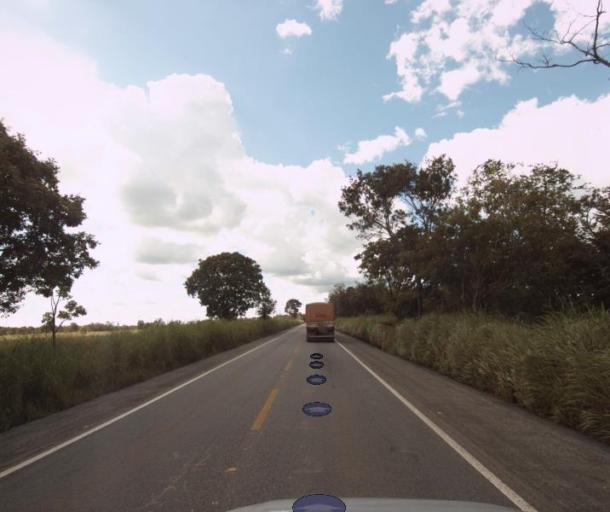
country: BR
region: Goias
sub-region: Porangatu
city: Porangatu
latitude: -13.2242
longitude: -49.1477
